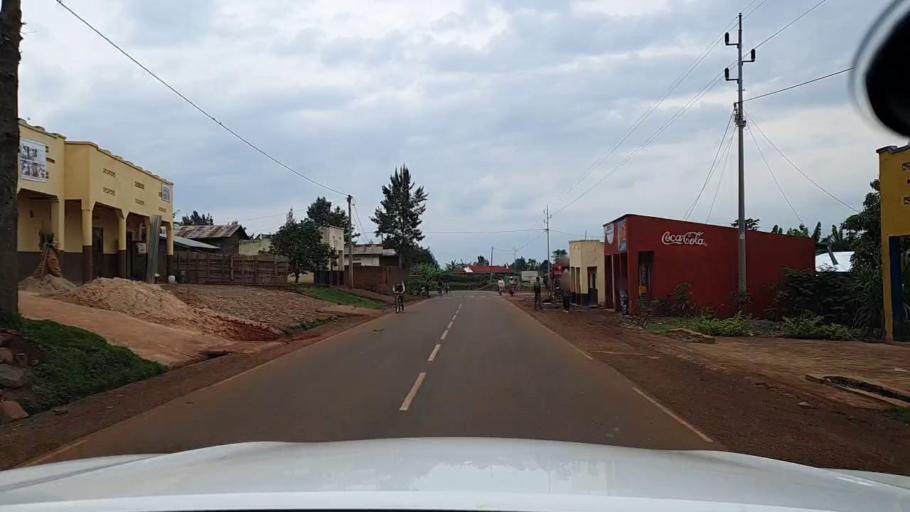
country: RW
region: Western Province
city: Cyangugu
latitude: -2.6434
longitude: 28.9536
